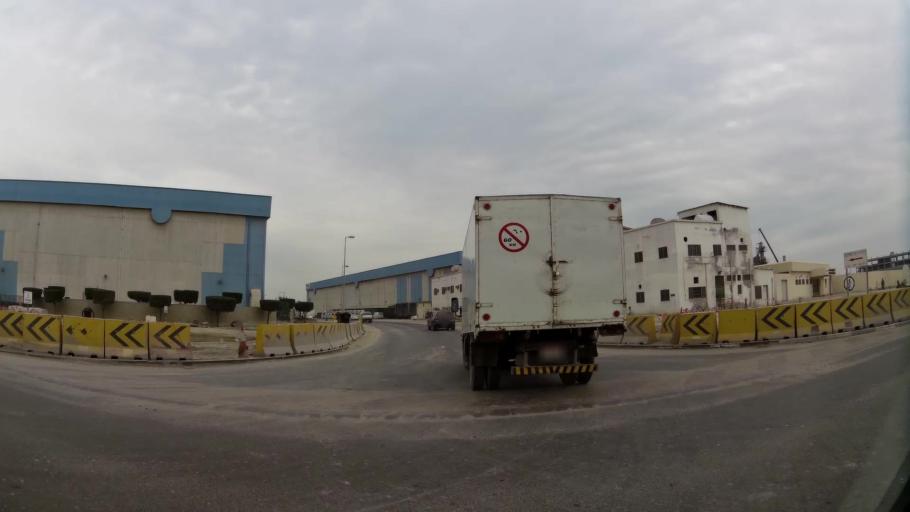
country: BH
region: Northern
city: Sitrah
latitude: 26.1290
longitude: 50.6020
